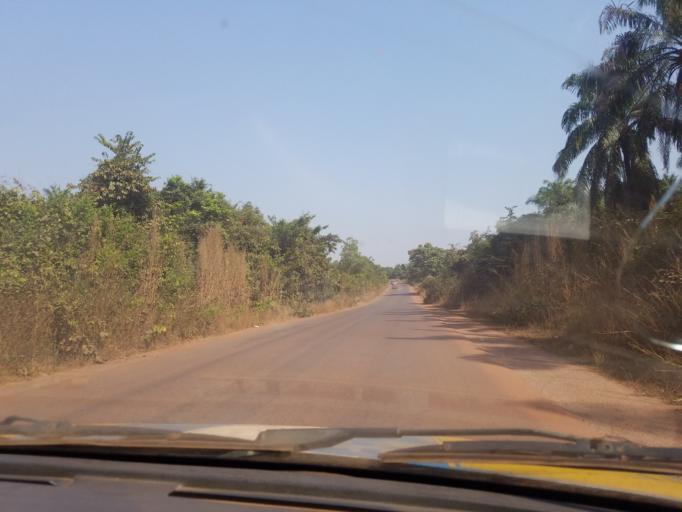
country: GN
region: Boke
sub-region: Boke Prefecture
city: Boke
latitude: 10.8345
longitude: -14.3611
